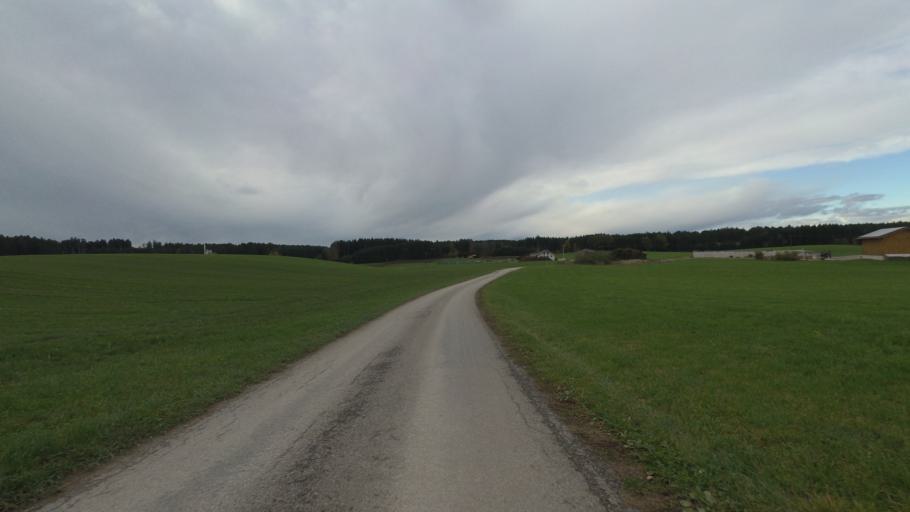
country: DE
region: Bavaria
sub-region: Upper Bavaria
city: Nussdorf
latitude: 47.9097
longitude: 12.5883
